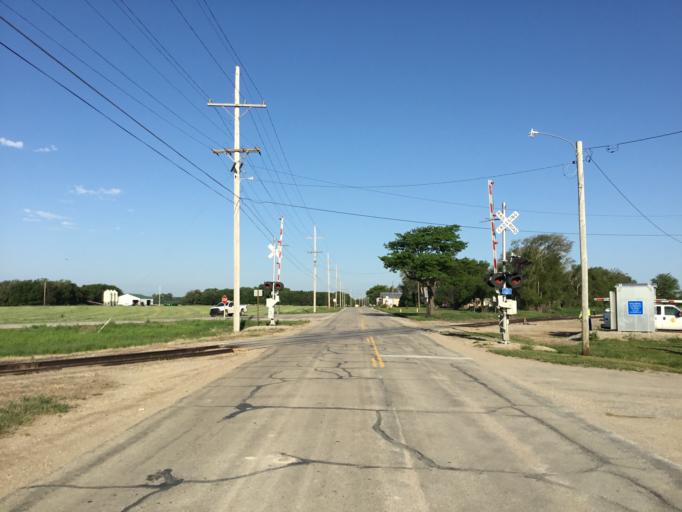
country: US
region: Kansas
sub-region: Mitchell County
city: Beloit
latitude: 39.4516
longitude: -98.0920
